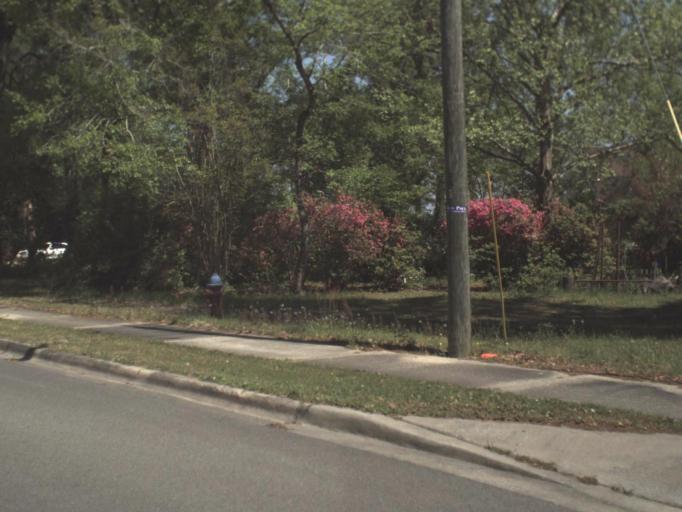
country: US
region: Florida
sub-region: Okaloosa County
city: Valparaiso
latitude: 30.5160
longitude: -86.4956
